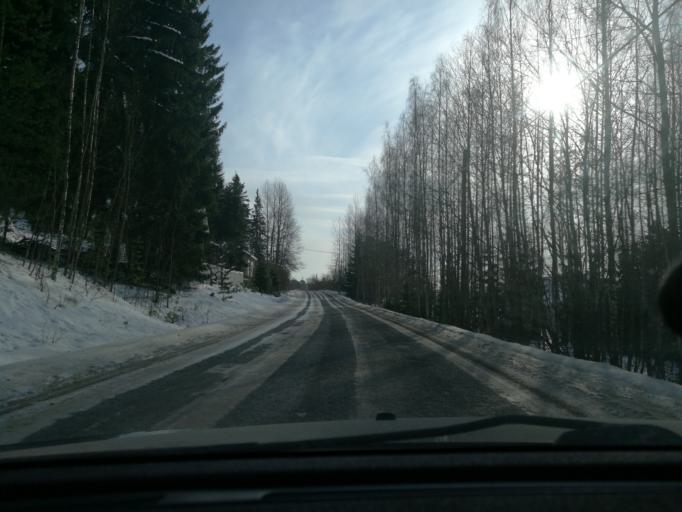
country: FI
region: Uusimaa
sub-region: Helsinki
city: Saukkola
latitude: 60.4687
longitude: 23.9876
